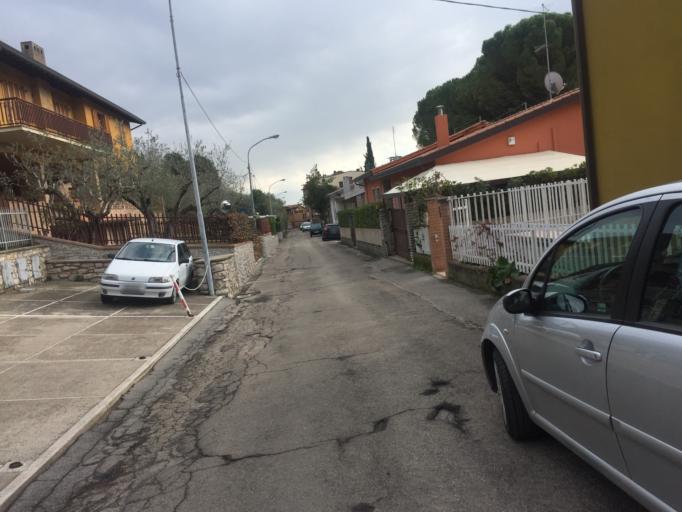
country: IT
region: Umbria
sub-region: Provincia di Perugia
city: Perugia
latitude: 43.1182
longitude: 12.4058
